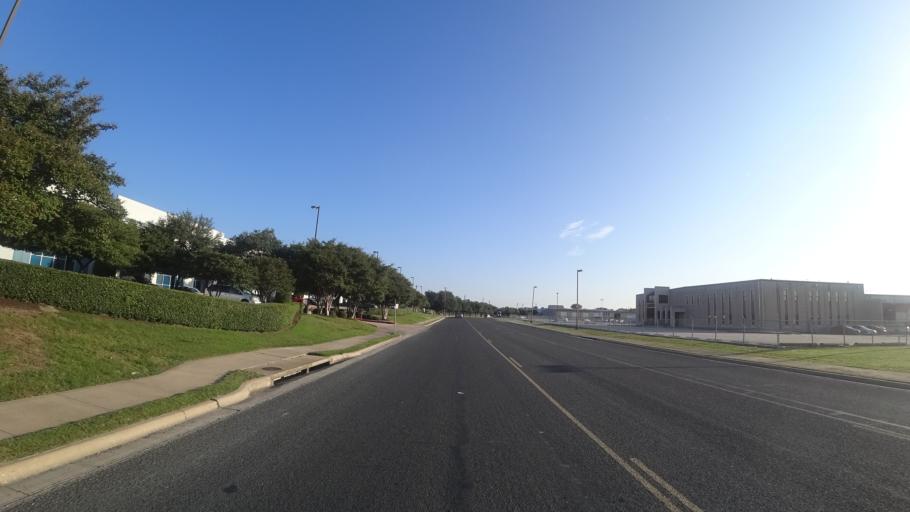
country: US
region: Texas
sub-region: Travis County
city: Manor
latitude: 30.3322
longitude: -97.6594
